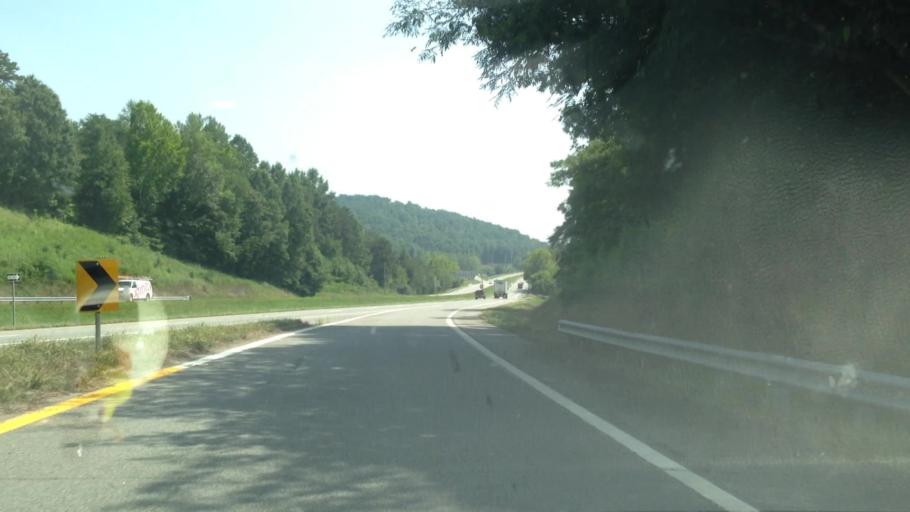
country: US
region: Virginia
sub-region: Henry County
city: Stanleytown
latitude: 36.7353
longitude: -79.9376
